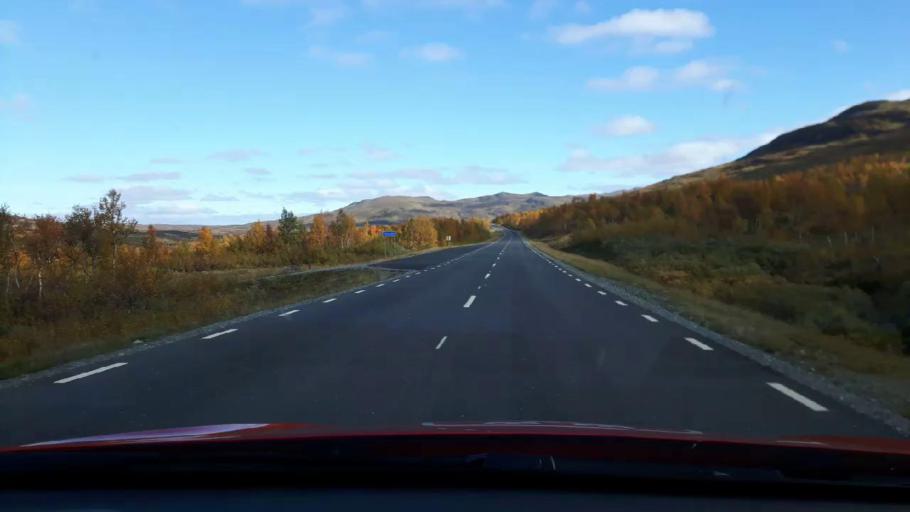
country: NO
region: Nordland
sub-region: Hattfjelldal
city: Hattfjelldal
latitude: 65.0107
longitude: 14.2743
